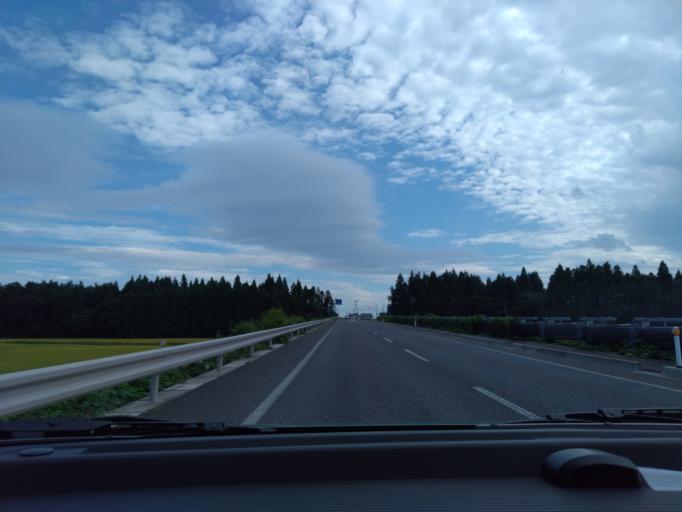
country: JP
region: Iwate
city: Hanamaki
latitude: 39.3762
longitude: 141.0564
